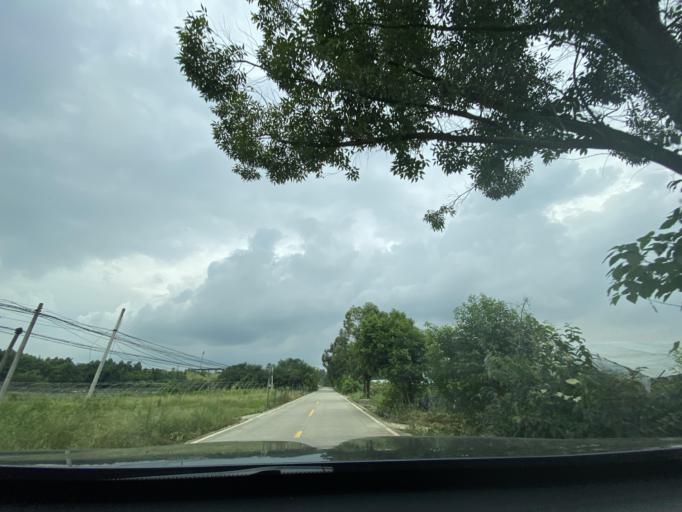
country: CN
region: Sichuan
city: Wujin
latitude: 30.3885
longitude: 103.9672
